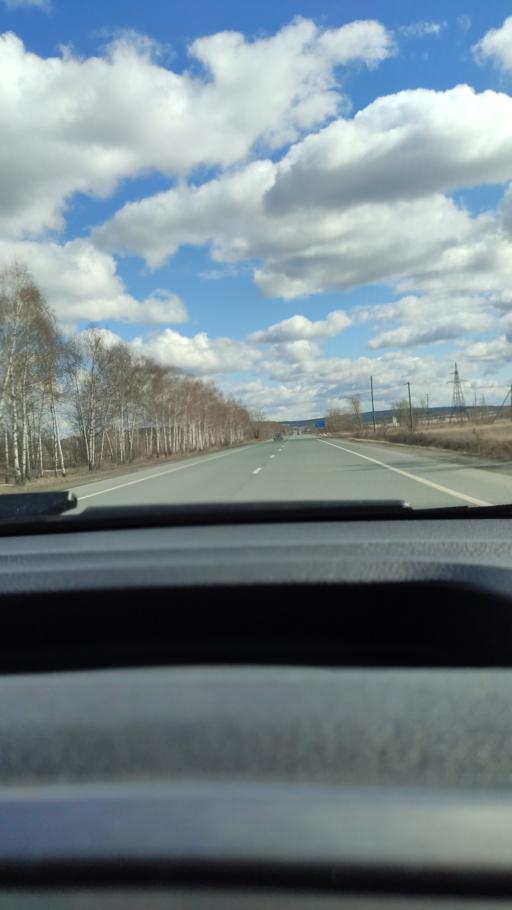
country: RU
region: Samara
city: Kurumoch
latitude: 53.4894
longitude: 49.9890
